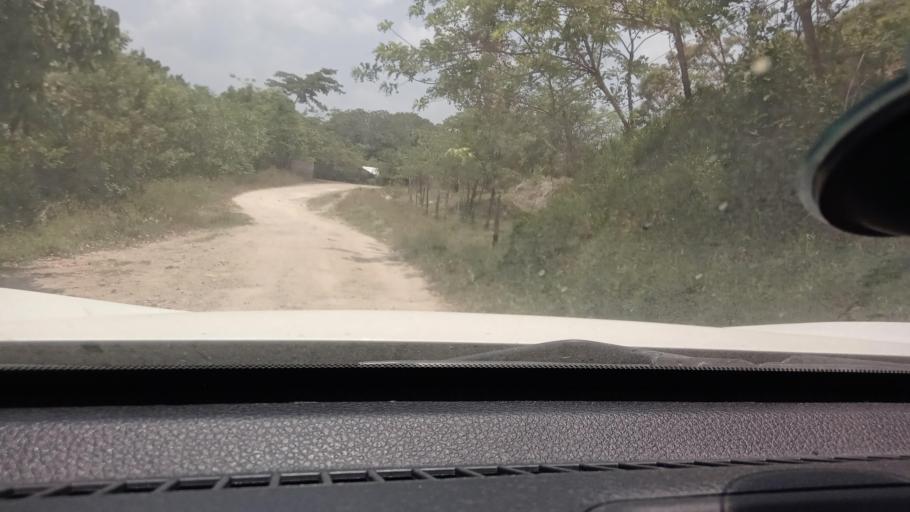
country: MX
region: Tabasco
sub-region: Huimanguillo
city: Francisco Rueda
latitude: 17.4978
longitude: -93.9069
